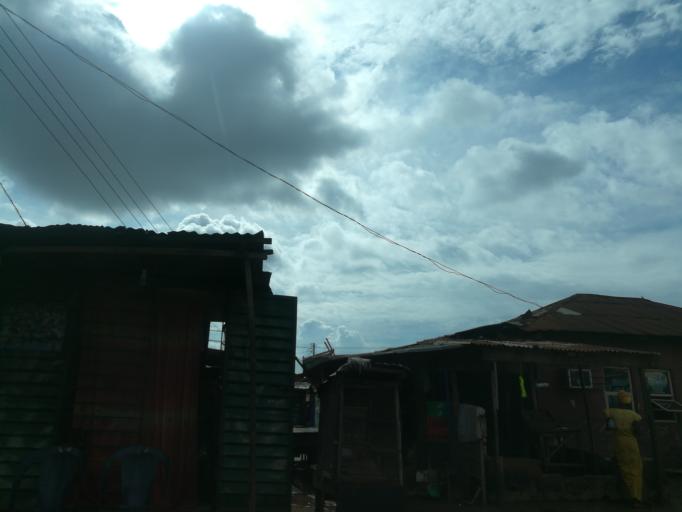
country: NG
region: Lagos
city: Ikorodu
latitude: 6.5936
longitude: 3.5169
